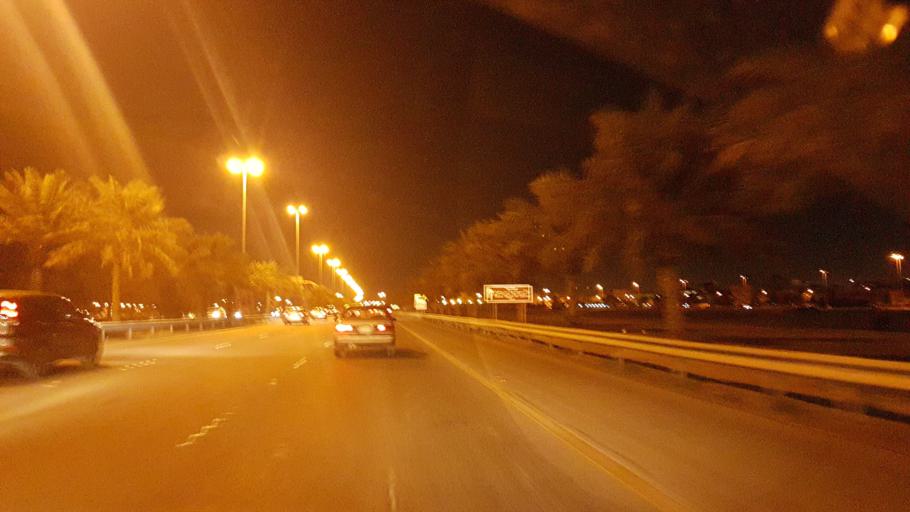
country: BH
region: Muharraq
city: Al Hadd
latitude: 26.2513
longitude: 50.6593
